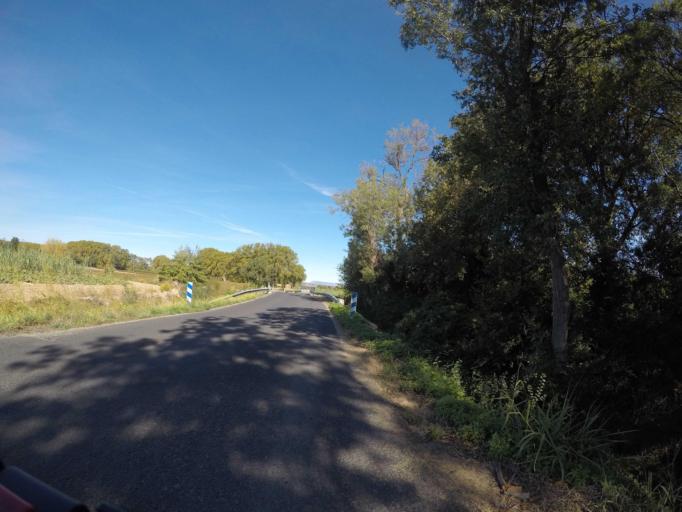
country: FR
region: Languedoc-Roussillon
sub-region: Departement des Pyrenees-Orientales
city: Le Soler
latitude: 42.6608
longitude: 2.7962
